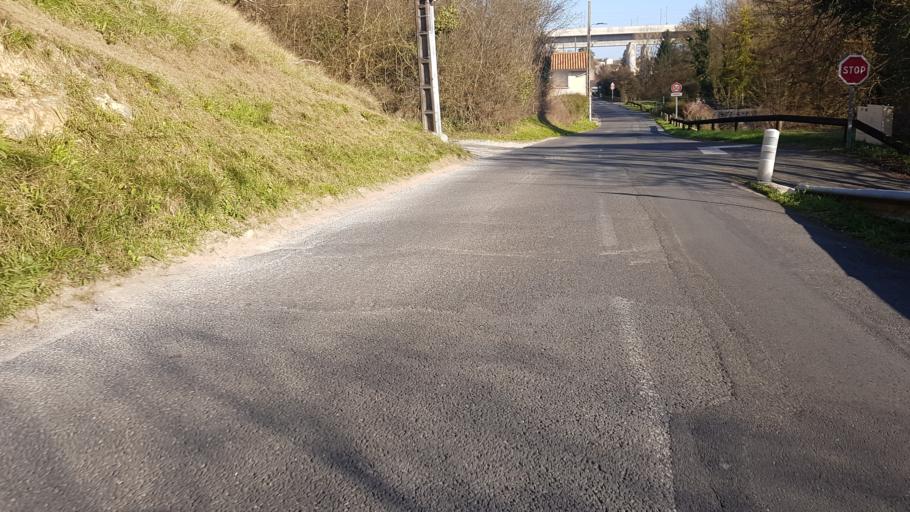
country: FR
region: Poitou-Charentes
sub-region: Departement de la Vienne
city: Chasseneuil-du-Poitou
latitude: 46.6424
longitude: 0.3453
